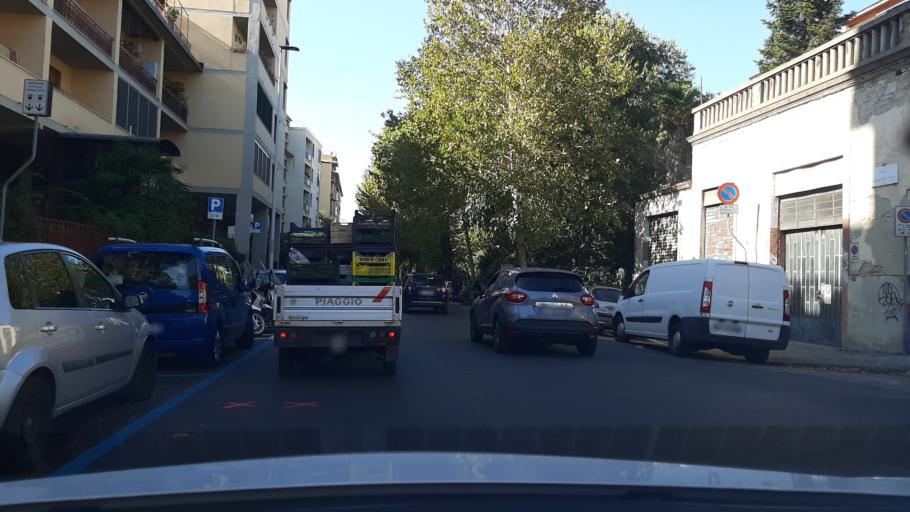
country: IT
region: Tuscany
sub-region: Province of Florence
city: Florence
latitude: 43.7850
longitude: 11.2734
